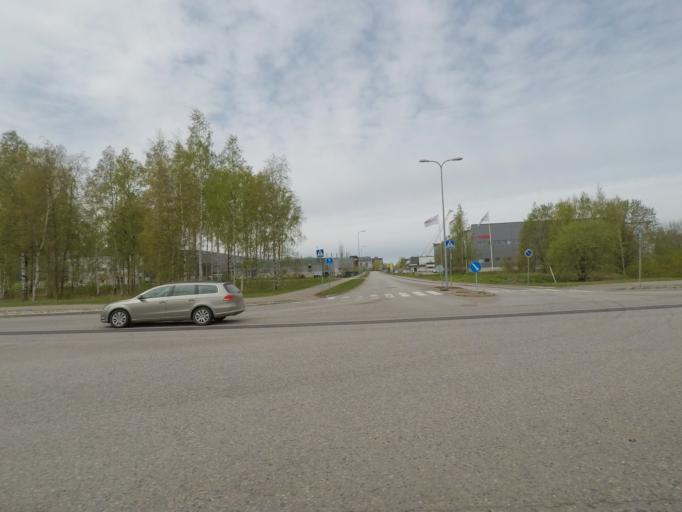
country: FI
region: Uusimaa
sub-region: Helsinki
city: Vantaa
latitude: 60.2910
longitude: 24.9973
